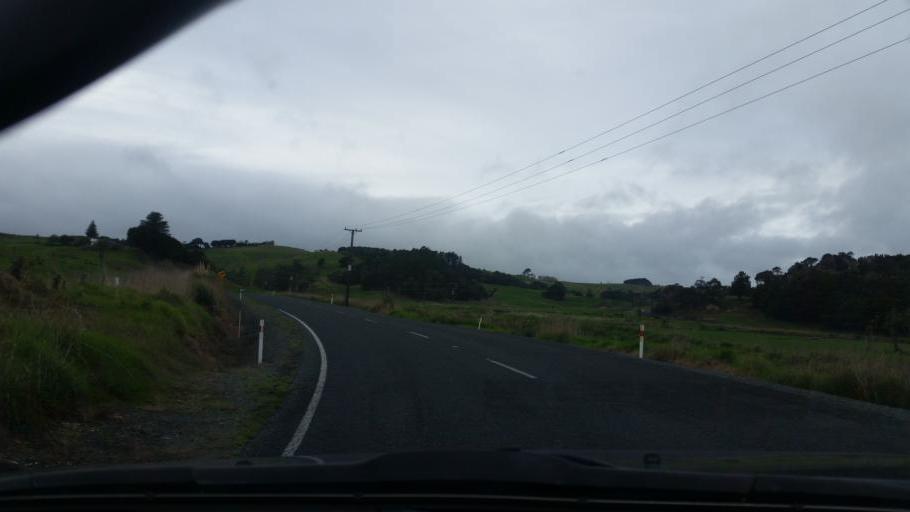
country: NZ
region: Northland
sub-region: Kaipara District
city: Dargaville
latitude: -36.0061
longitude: 173.9616
